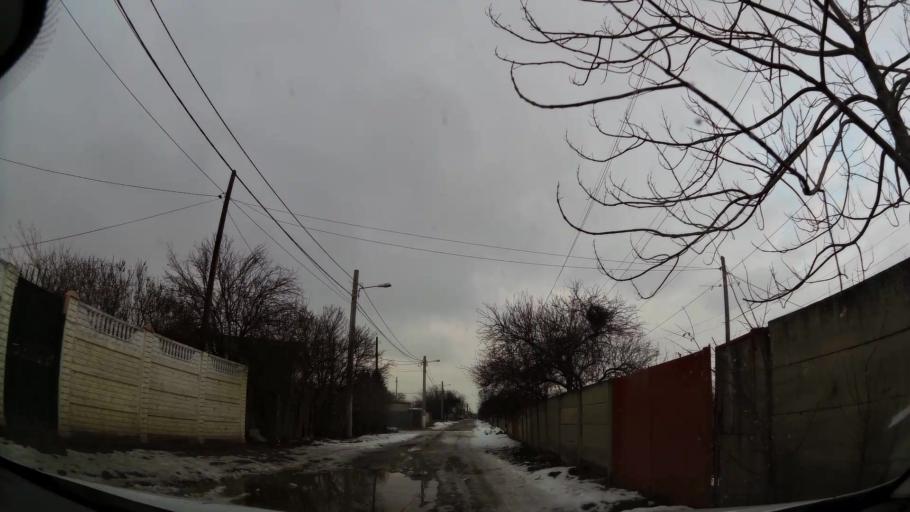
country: RO
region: Ilfov
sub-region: Voluntari City
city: Voluntari
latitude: 44.4804
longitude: 26.1858
